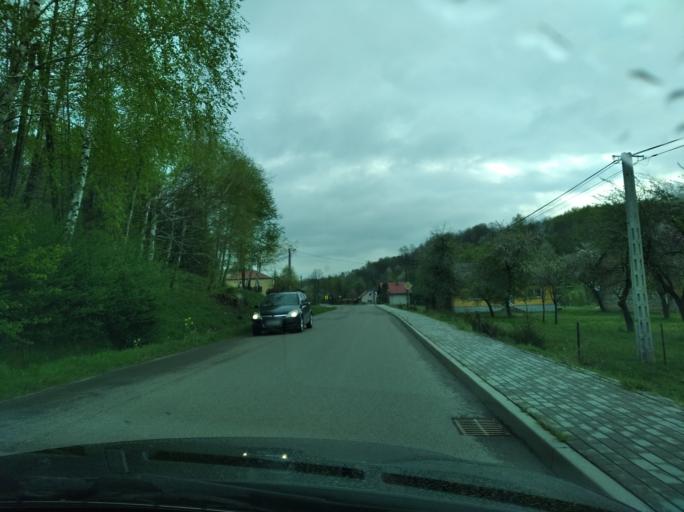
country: PL
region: Subcarpathian Voivodeship
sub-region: Powiat rzeszowski
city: Lecka
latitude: 49.8698
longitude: 22.0354
